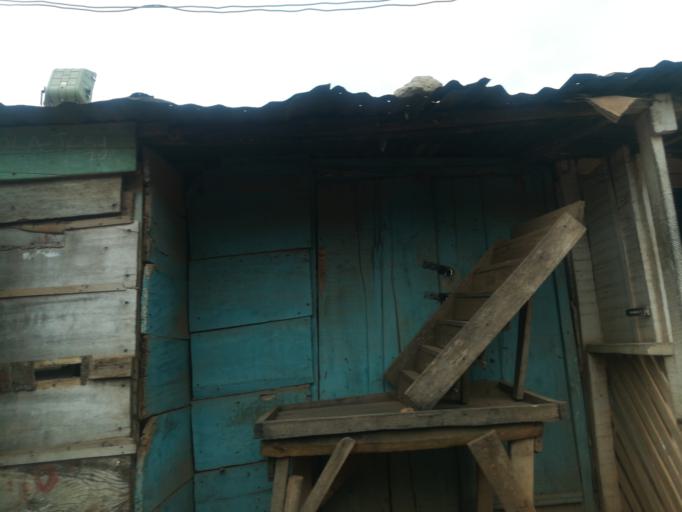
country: NG
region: Oyo
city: Ibadan
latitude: 7.3627
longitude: 3.9268
